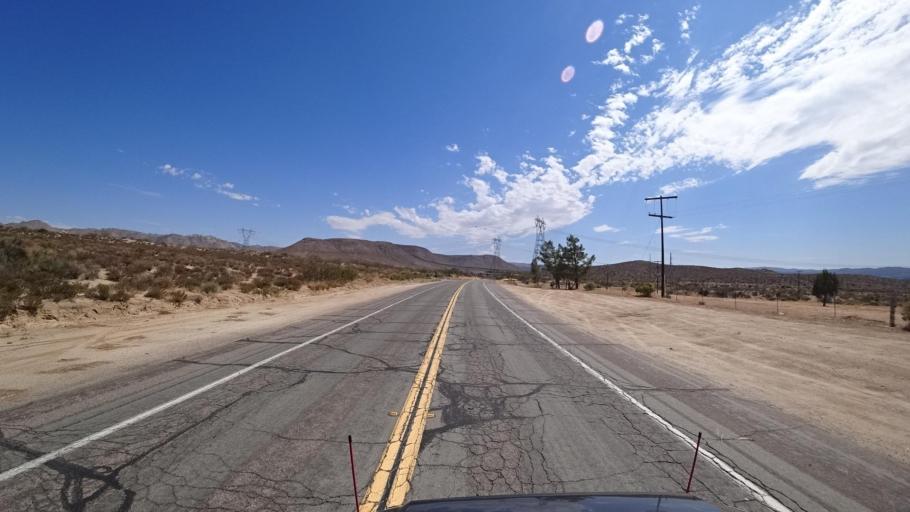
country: MX
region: Baja California
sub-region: Tecate
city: Cereso del Hongo
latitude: 32.6335
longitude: -116.1647
